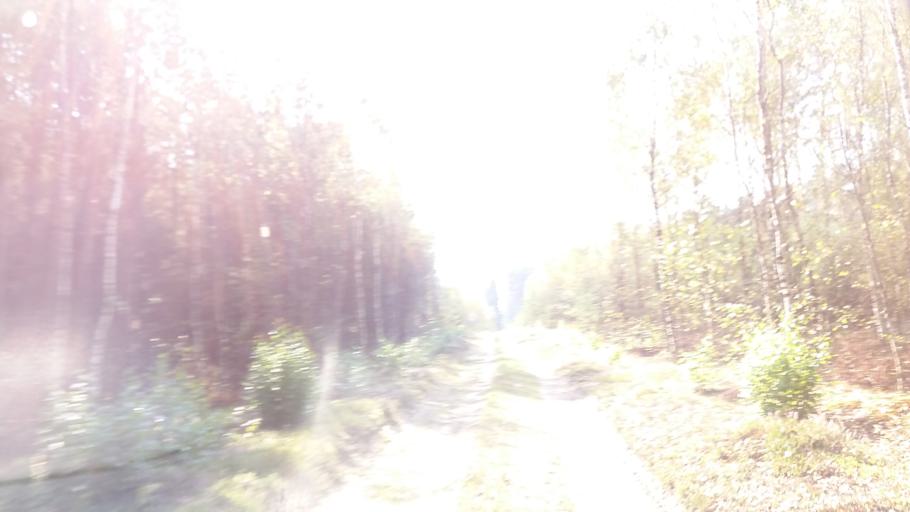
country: PL
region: West Pomeranian Voivodeship
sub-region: Powiat drawski
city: Kalisz Pomorski
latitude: 53.2102
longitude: 15.8967
